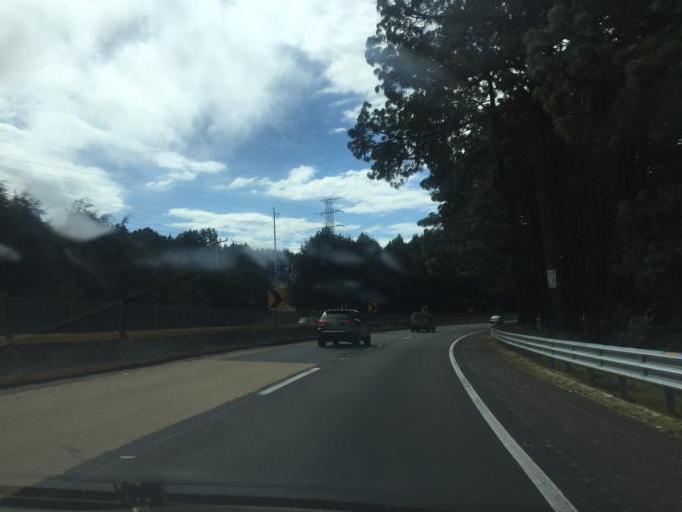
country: MX
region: Morelos
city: Tres Marias
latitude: 19.0663
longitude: -99.2380
